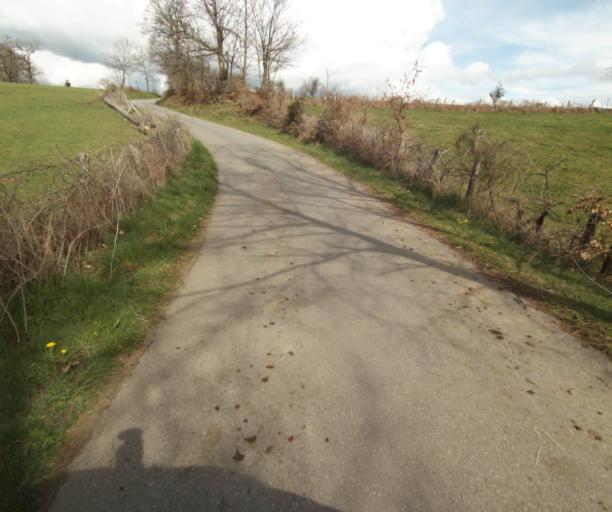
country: FR
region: Limousin
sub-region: Departement de la Correze
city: Correze
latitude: 45.3636
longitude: 1.8986
